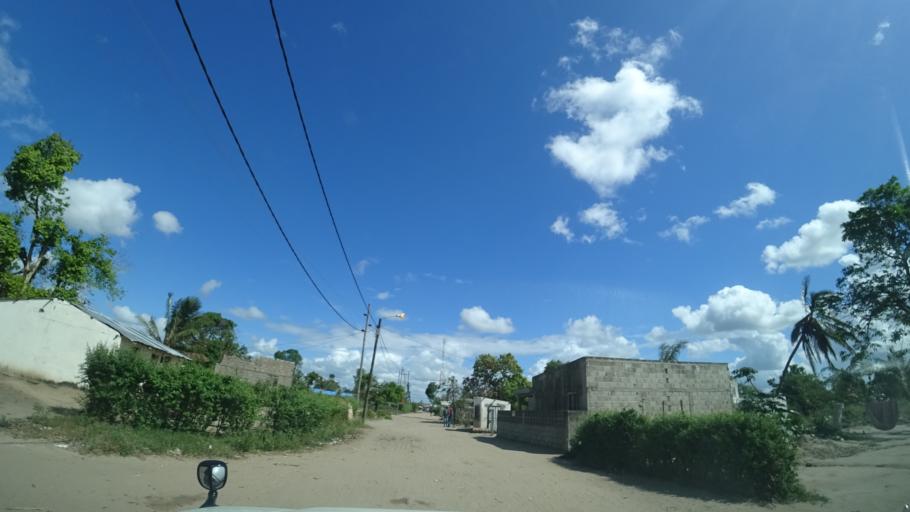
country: MZ
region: Sofala
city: Dondo
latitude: -19.4987
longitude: 34.5978
